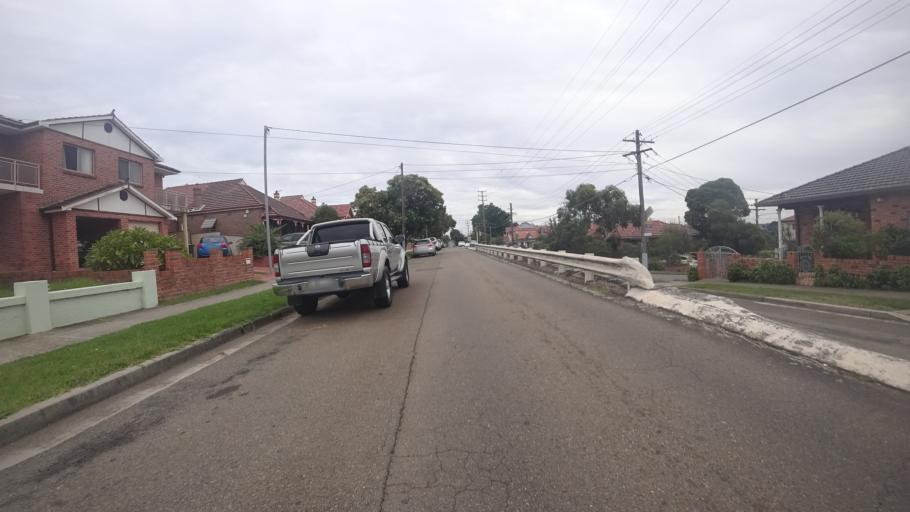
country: AU
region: New South Wales
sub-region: Rockdale
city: Bardwell Valley
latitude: -33.9393
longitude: 151.1322
